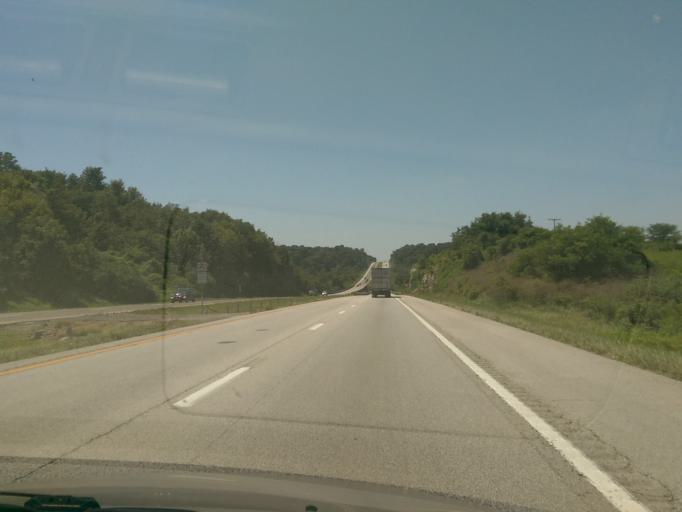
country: US
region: Missouri
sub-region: Cooper County
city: Boonville
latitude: 38.9343
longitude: -92.9365
